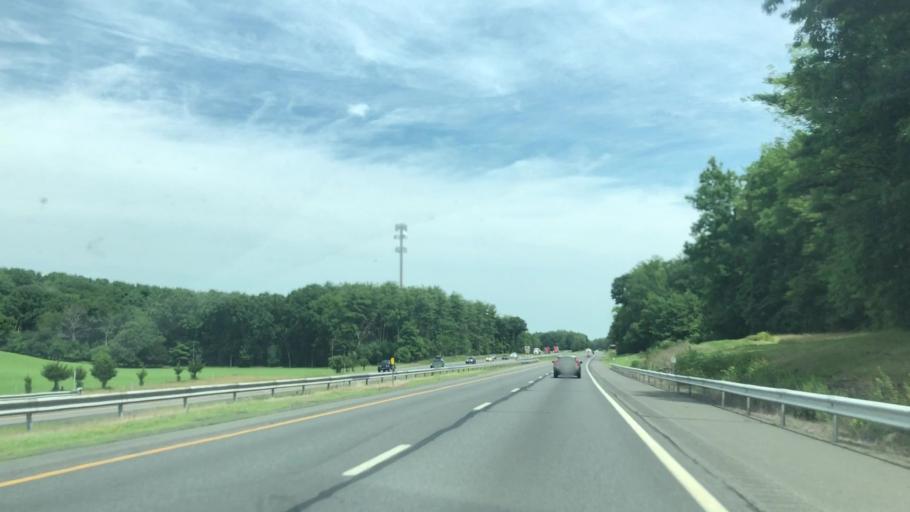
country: US
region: New York
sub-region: Greene County
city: Coxsackie
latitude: 42.3252
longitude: -73.8641
